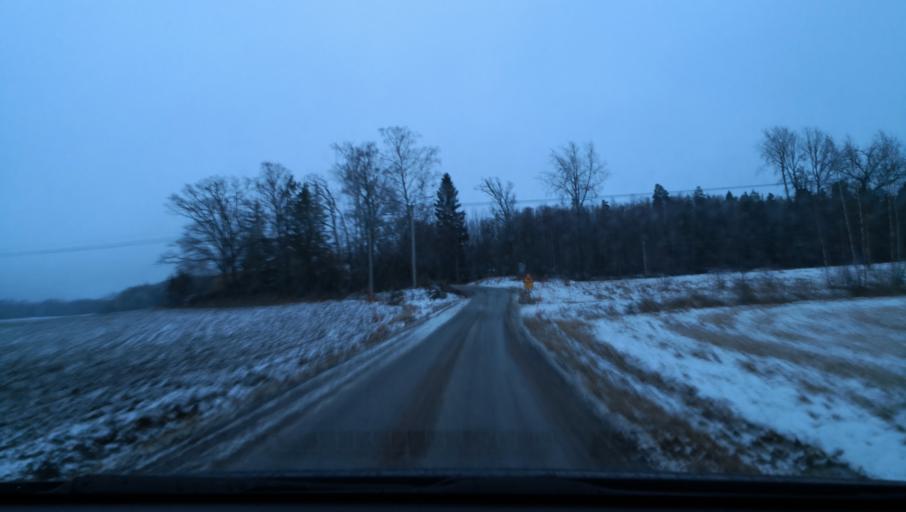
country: SE
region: Vaestmanland
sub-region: Kungsors Kommun
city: Kungsoer
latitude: 59.4078
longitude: 16.2031
